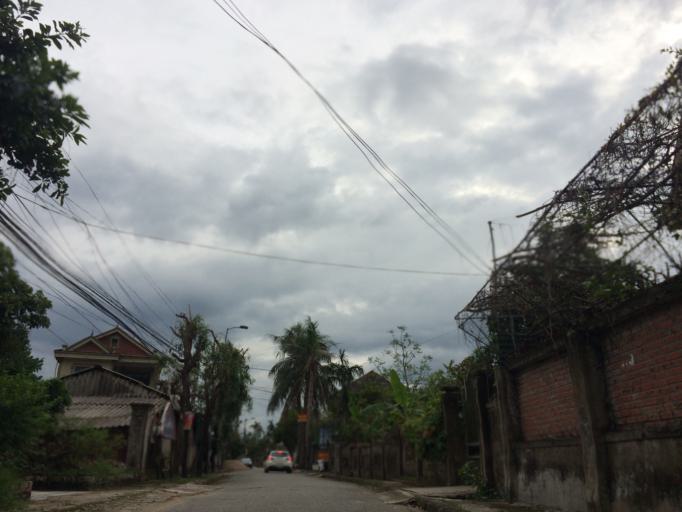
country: VN
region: Ha Tinh
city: Ha Tinh
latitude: 18.3458
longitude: 105.8861
